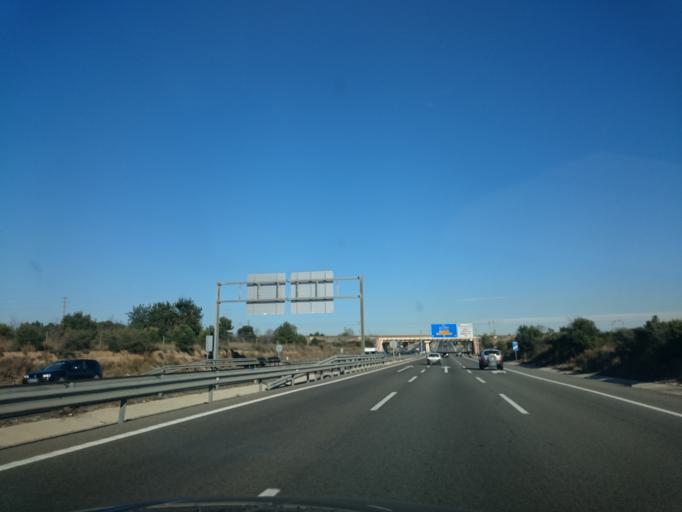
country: ES
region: Catalonia
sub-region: Provincia de Tarragona
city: Vila-seca
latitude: 41.1097
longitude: 1.1568
